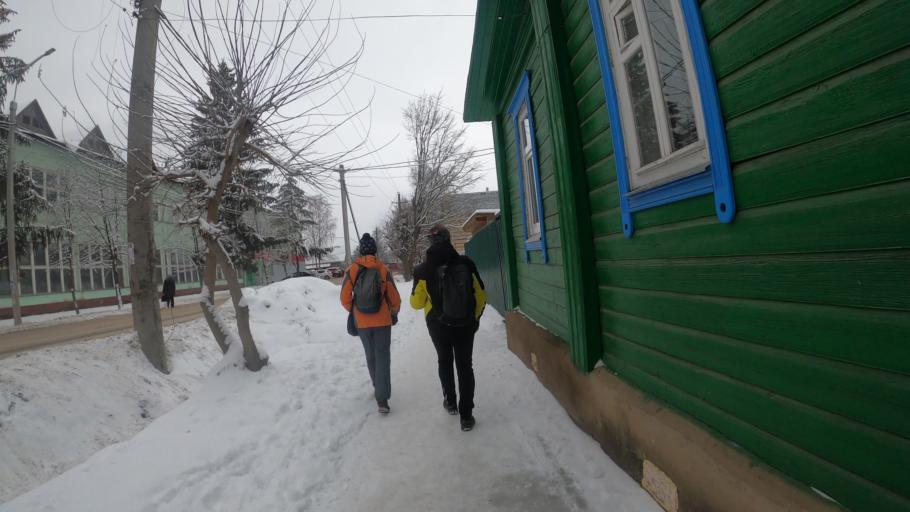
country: RU
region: Jaroslavl
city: Pereslavl'-Zalesskiy
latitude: 56.7383
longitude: 38.8449
